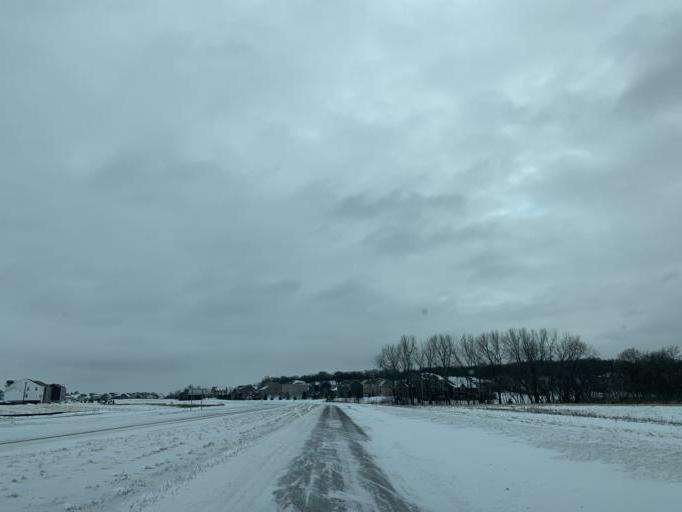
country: US
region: Minnesota
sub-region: Washington County
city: Cottage Grove
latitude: 44.8565
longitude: -92.9237
